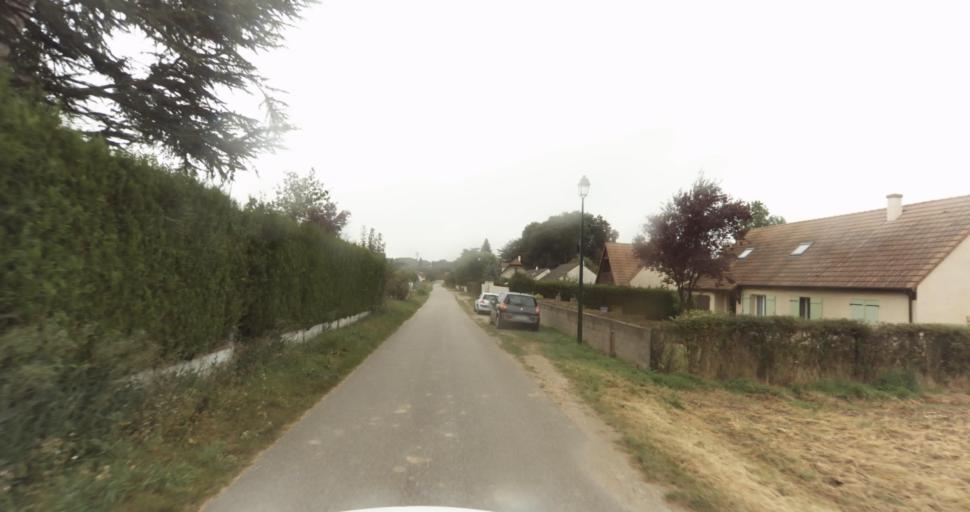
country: FR
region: Haute-Normandie
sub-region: Departement de l'Eure
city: Saint-Germain-sur-Avre
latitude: 48.7592
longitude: 1.2574
